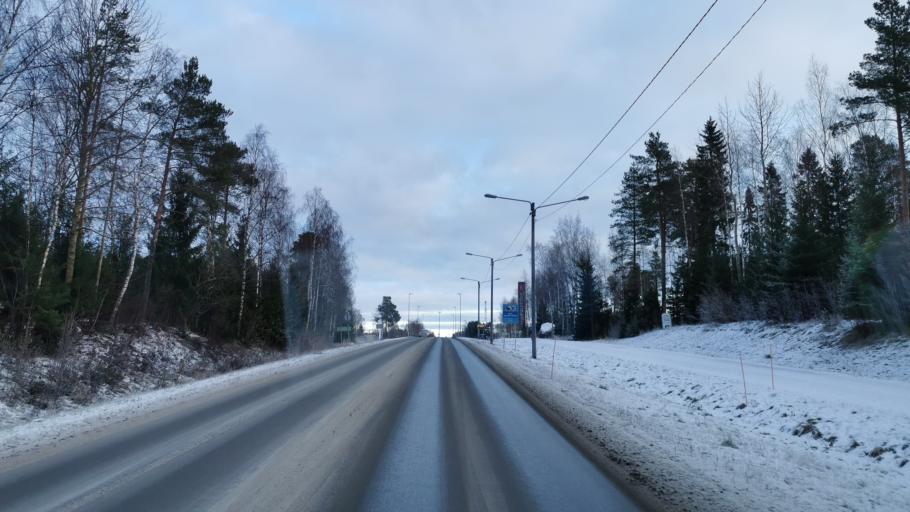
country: FI
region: Ostrobothnia
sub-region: Vaasa
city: Korsholm
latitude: 63.1114
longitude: 21.6718
